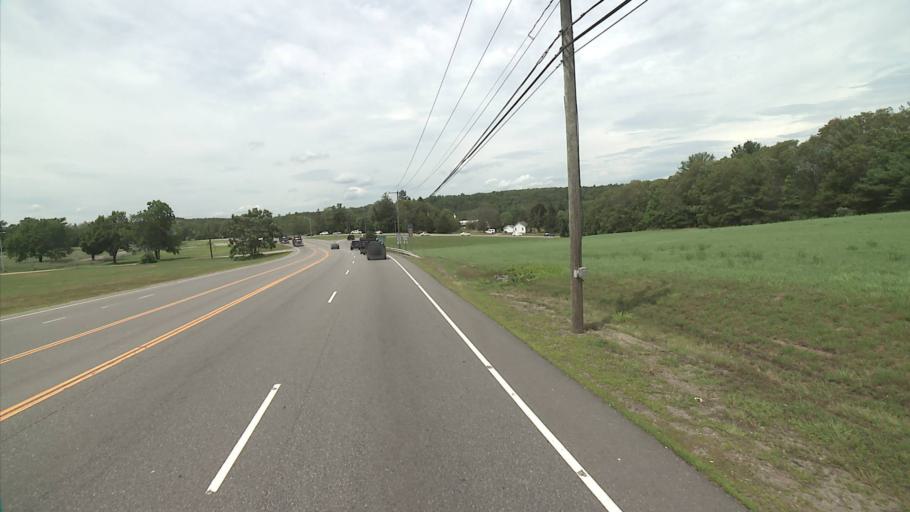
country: US
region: Connecticut
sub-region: New London County
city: Norwich
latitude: 41.4846
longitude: -72.0660
